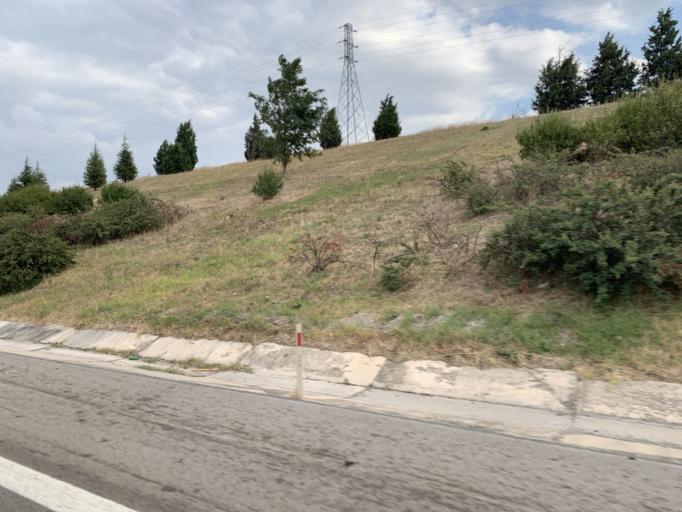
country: TR
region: Bursa
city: Gorukle
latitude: 40.2586
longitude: 28.8348
